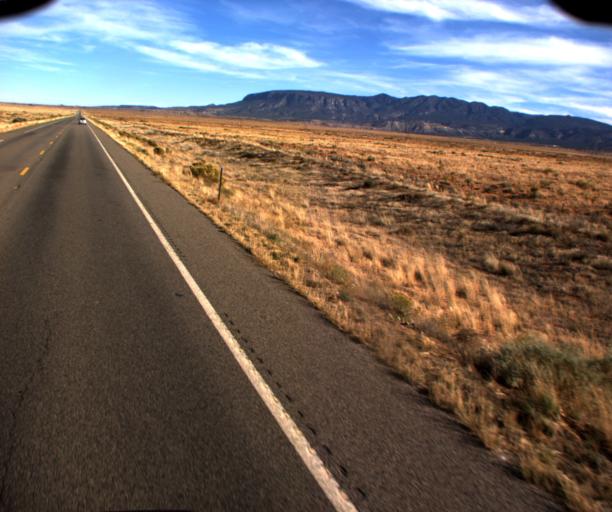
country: US
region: Arizona
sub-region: Apache County
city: Lukachukai
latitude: 36.9476
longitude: -109.2738
